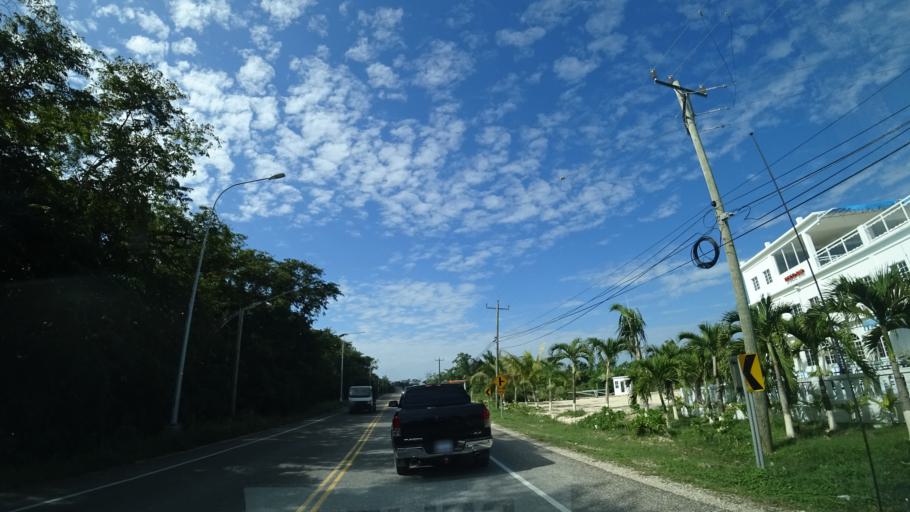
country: BZ
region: Belize
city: Belize City
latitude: 17.5444
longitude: -88.2587
